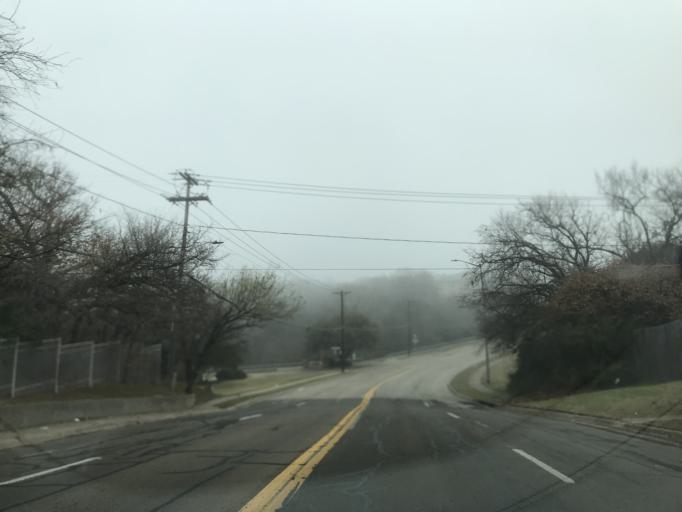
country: US
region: Texas
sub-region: Tarrant County
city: Arlington
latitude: 32.7744
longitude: -97.0887
